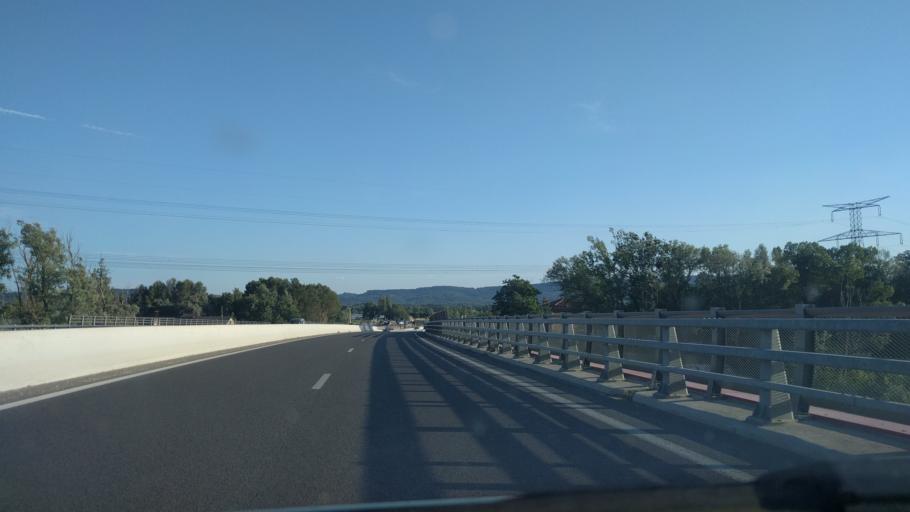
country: FR
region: Provence-Alpes-Cote d'Azur
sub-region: Departement du Vaucluse
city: Pertuis
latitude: 43.6667
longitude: 5.4963
